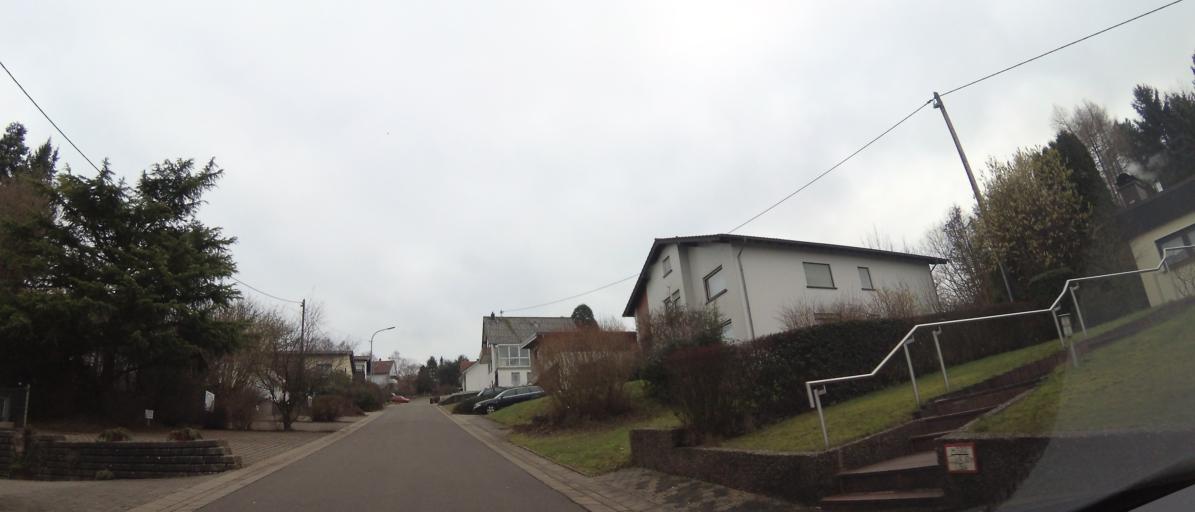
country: DE
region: Saarland
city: Illingen
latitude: 49.3894
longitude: 7.0755
